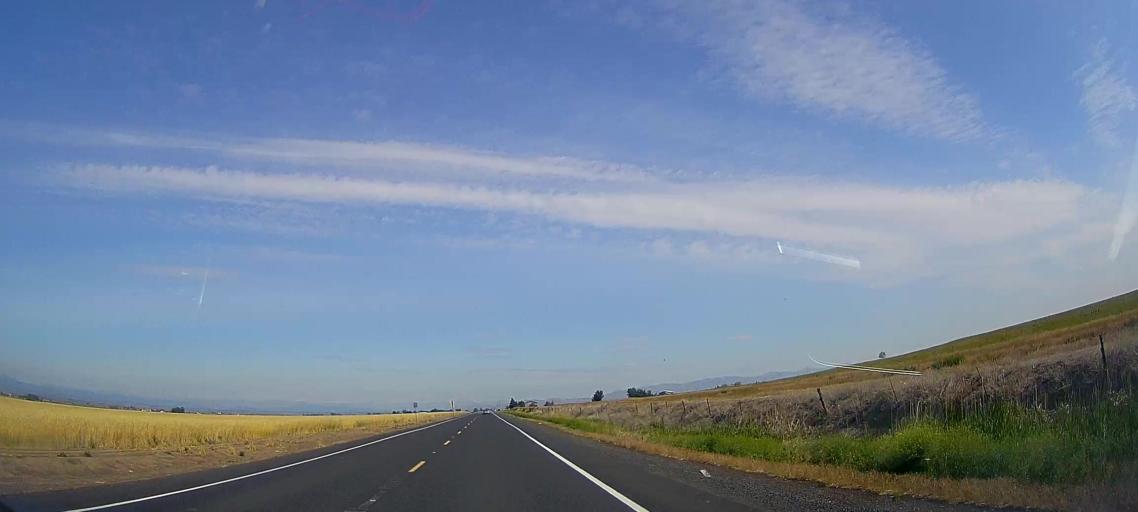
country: US
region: Oregon
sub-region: Jefferson County
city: Madras
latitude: 44.6701
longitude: -121.1398
